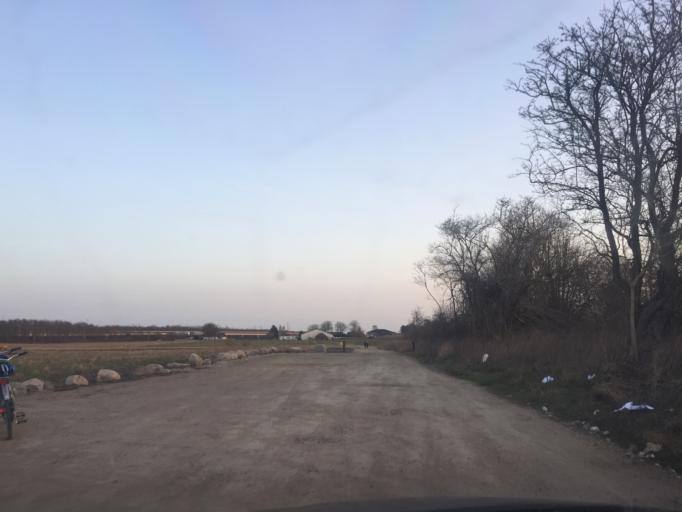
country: DK
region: Capital Region
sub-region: Ishoj Kommune
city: Ishoj
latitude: 55.6382
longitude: 12.3289
